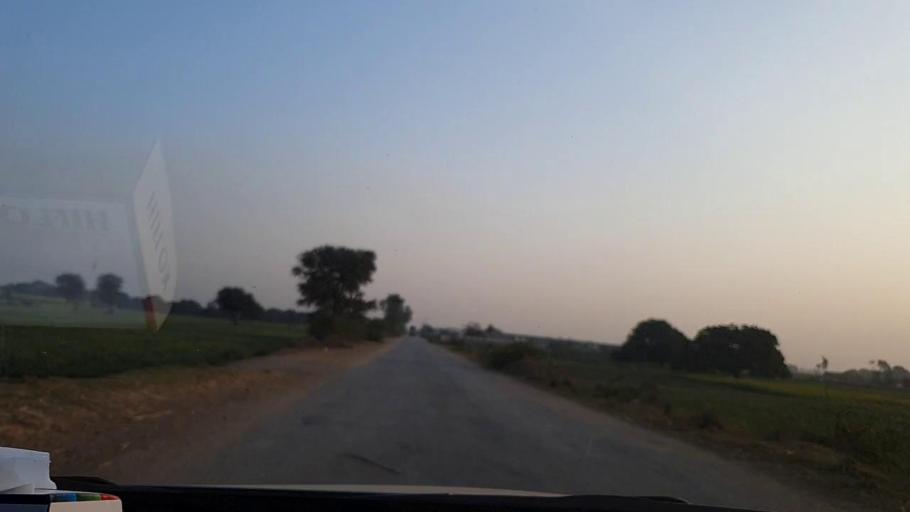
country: PK
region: Sindh
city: Tando Ghulam Ali
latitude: 25.1760
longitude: 68.9490
